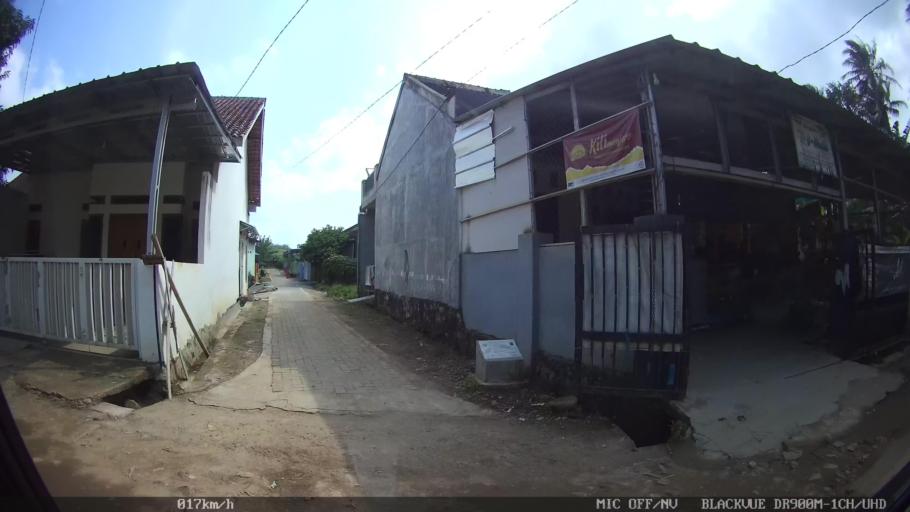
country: ID
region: Lampung
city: Kedaton
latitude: -5.3303
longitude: 105.2863
